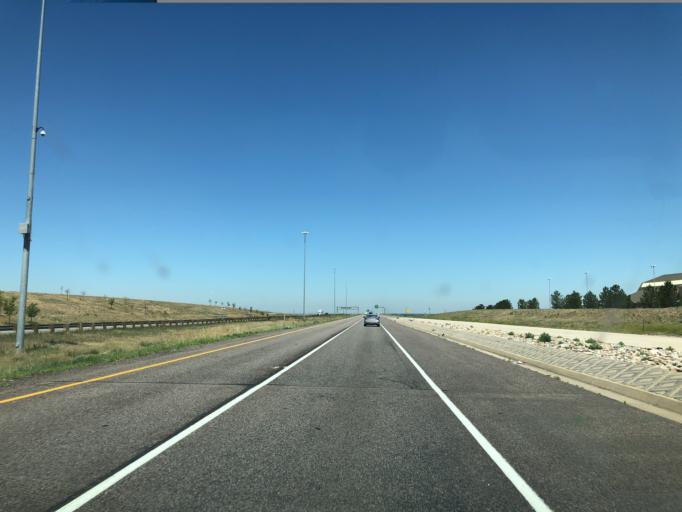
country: US
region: Colorado
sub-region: Adams County
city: Brighton
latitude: 39.8611
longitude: -104.7498
